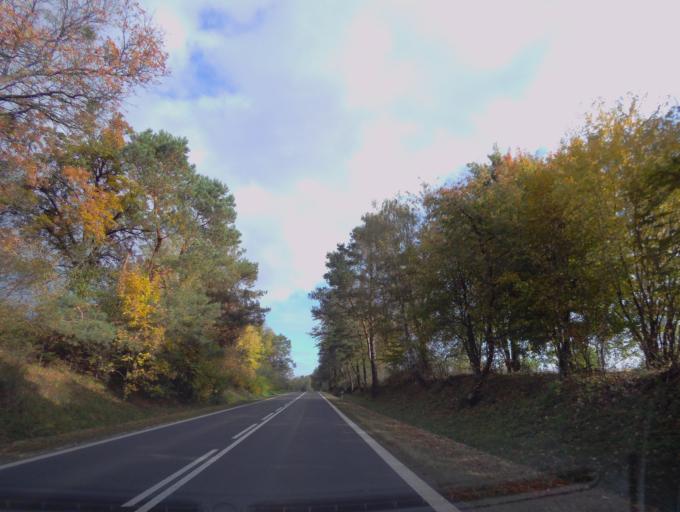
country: PL
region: Lublin Voivodeship
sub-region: Powiat bilgorajski
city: Turobin
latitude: 50.8161
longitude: 22.6973
